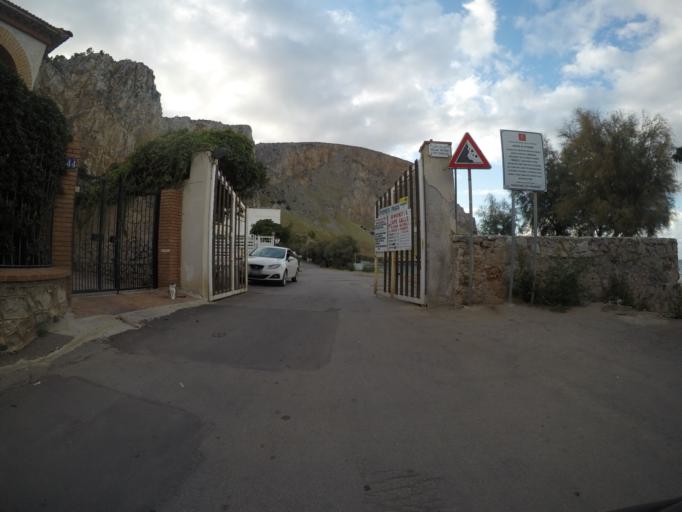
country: IT
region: Sicily
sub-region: Palermo
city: Palermo
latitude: 38.2115
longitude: 13.3274
